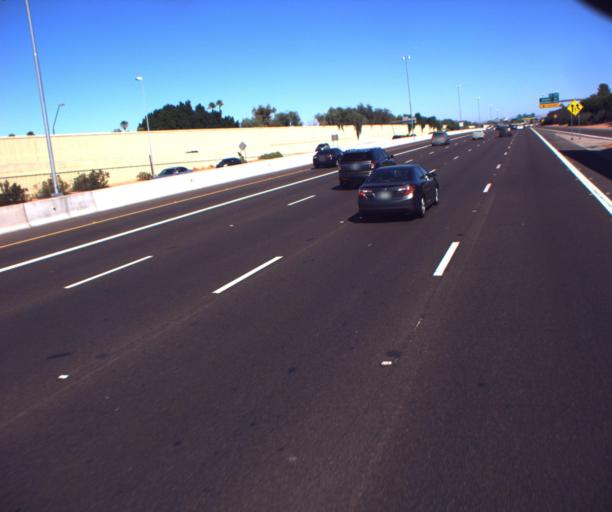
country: US
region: Arizona
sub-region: Maricopa County
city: San Carlos
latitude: 33.3671
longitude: -111.8936
